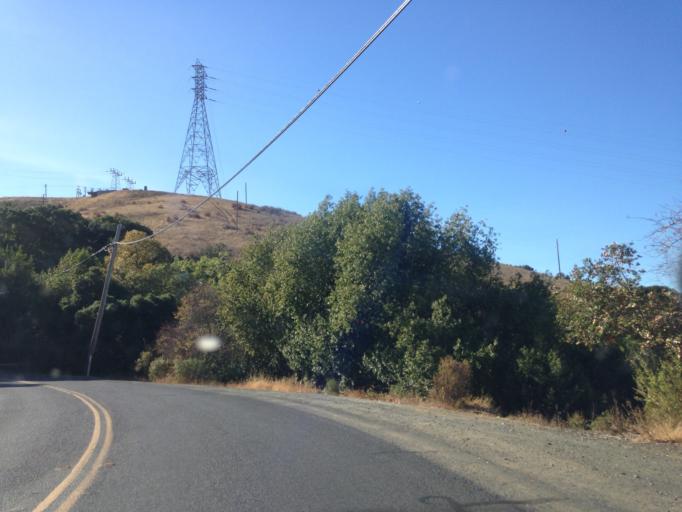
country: US
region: California
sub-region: Contra Costa County
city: Crockett
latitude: 38.0503
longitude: -122.2014
